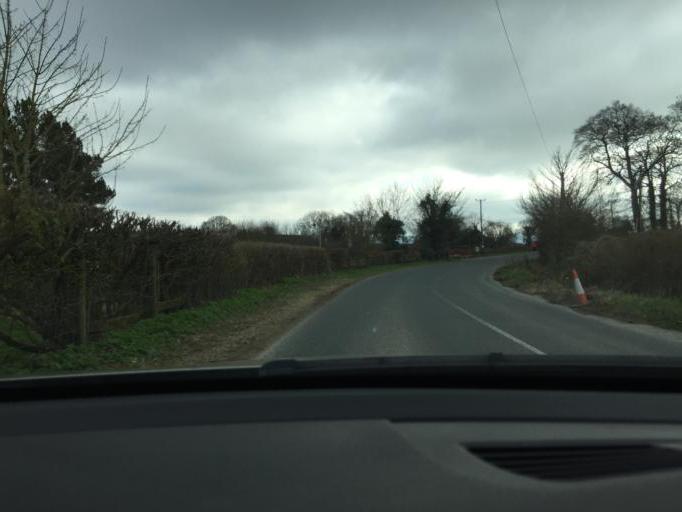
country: IE
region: Leinster
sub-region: Wicklow
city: Valleymount
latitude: 53.1309
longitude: -6.5256
